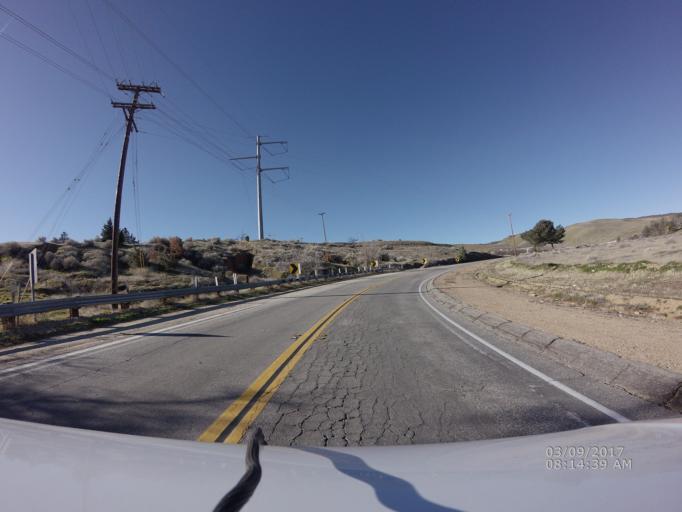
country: US
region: California
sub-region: Los Angeles County
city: Leona Valley
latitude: 34.6642
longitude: -118.3246
